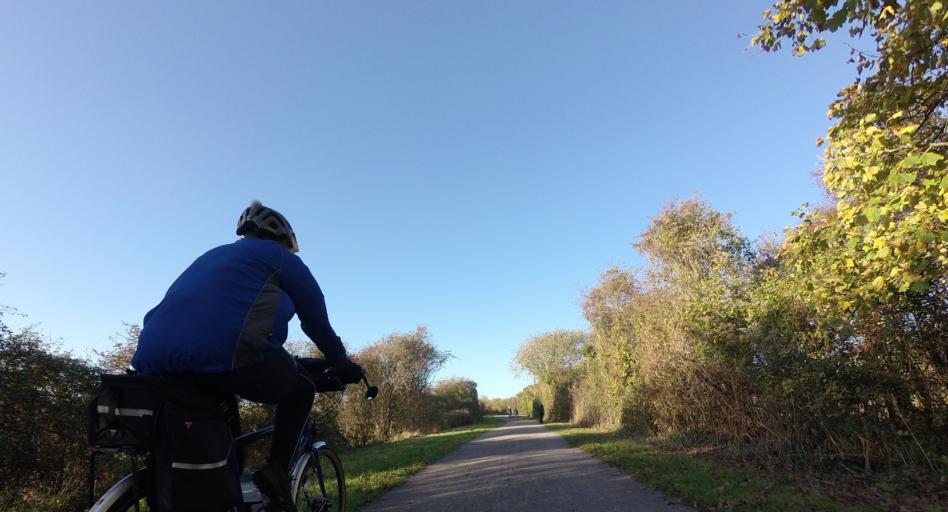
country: GB
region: England
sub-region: West Sussex
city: Shoreham-by-Sea
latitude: 50.8481
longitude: -0.2876
